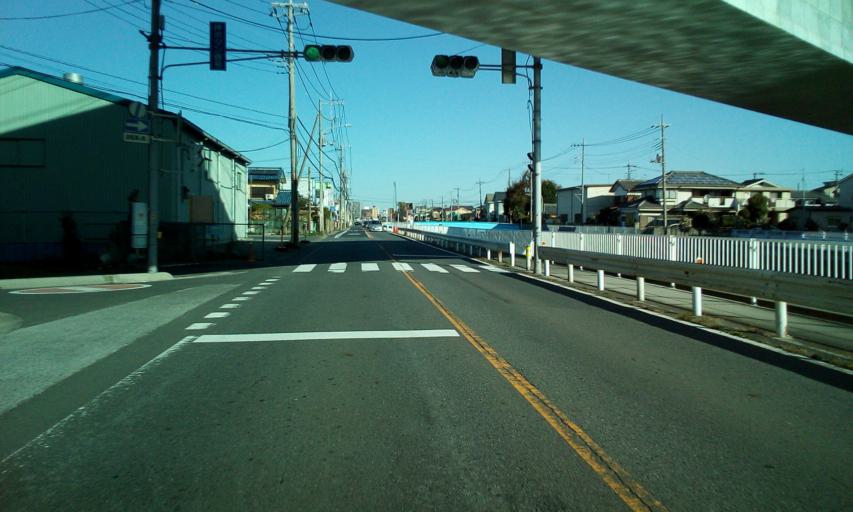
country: JP
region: Chiba
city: Nagareyama
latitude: 35.8300
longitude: 139.8831
